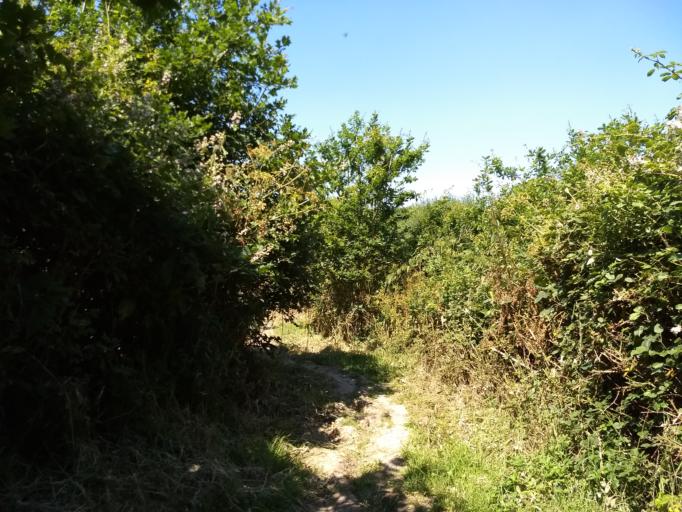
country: GB
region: England
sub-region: Isle of Wight
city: Gurnard
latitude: 50.7331
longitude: -1.3621
